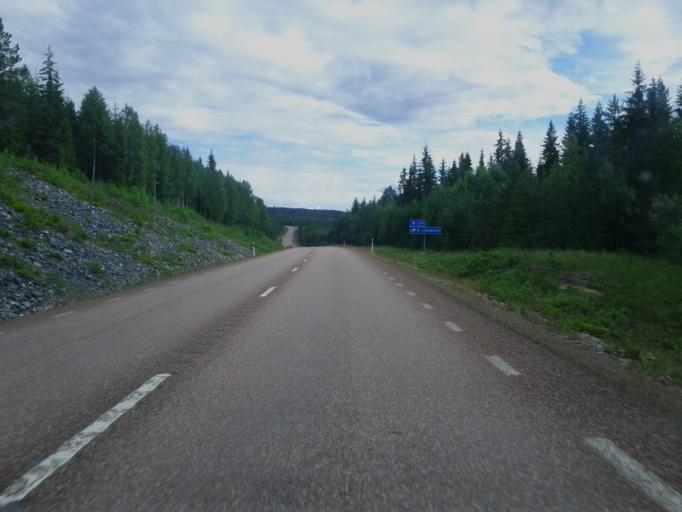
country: SE
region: Dalarna
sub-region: Rattviks Kommun
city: Raettvik
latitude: 60.7964
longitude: 15.2724
